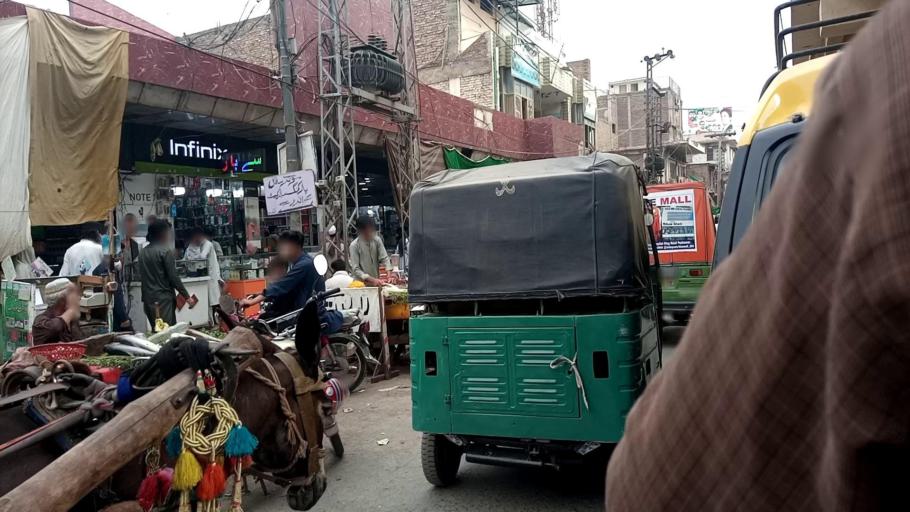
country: PK
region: Khyber Pakhtunkhwa
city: Peshawar
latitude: 34.0176
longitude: 71.5802
